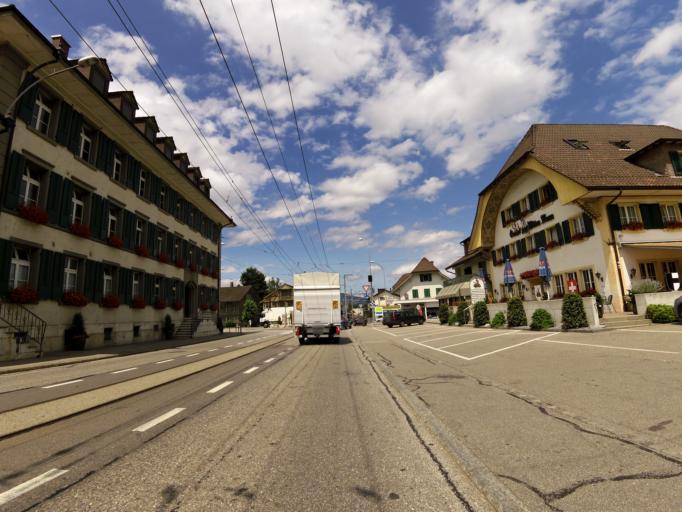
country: CH
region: Bern
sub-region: Oberaargau
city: Aarwangen
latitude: 47.2396
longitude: 7.7698
